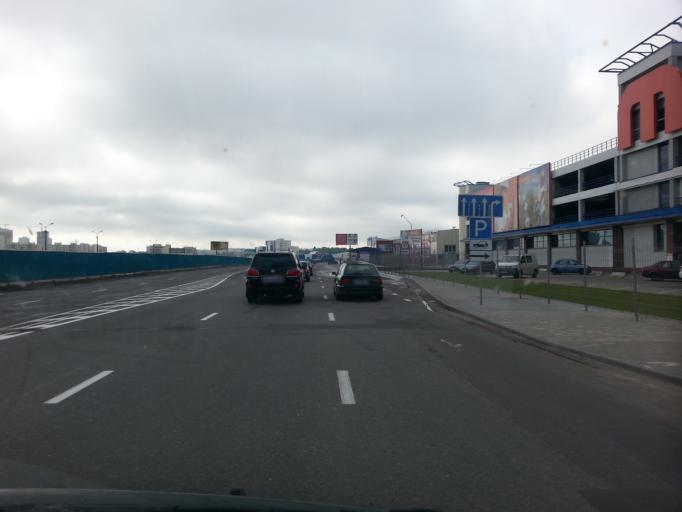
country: BY
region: Minsk
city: Zhdanovichy
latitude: 53.9388
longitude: 27.4441
